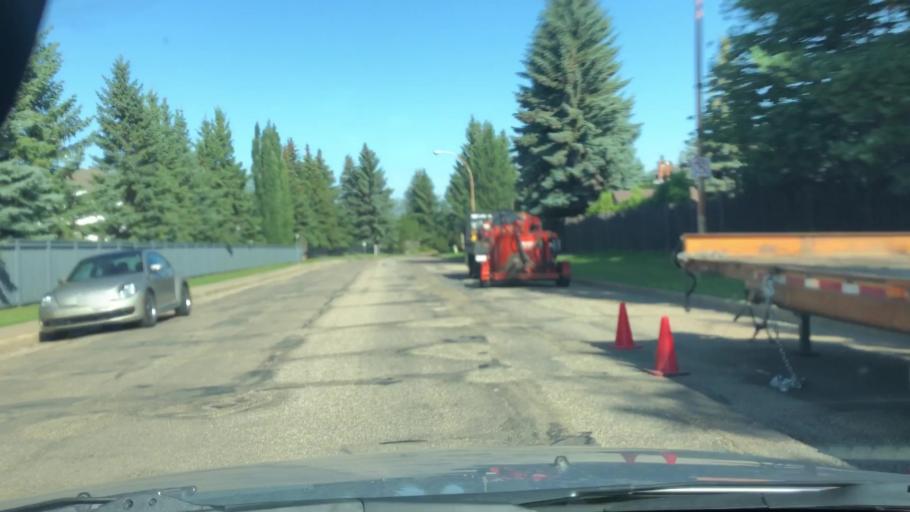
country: CA
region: Alberta
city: Edmonton
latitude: 53.4758
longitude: -113.6011
